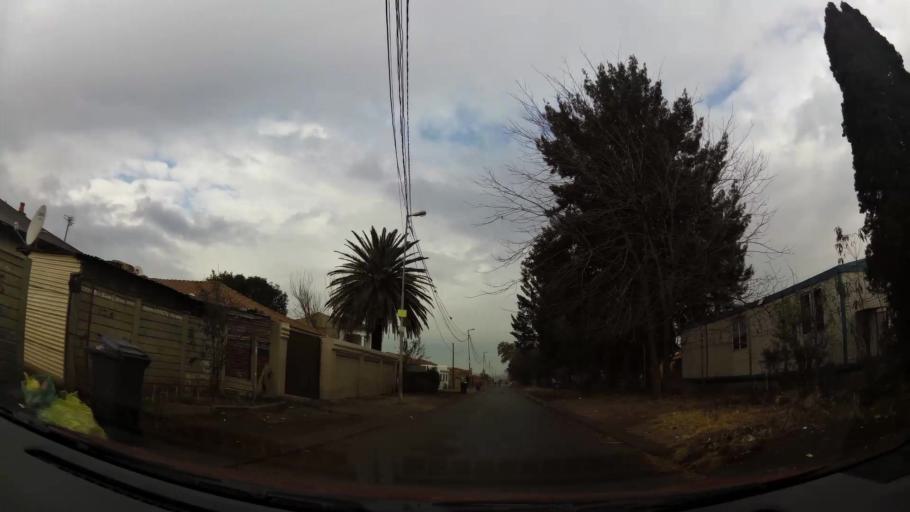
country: ZA
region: Gauteng
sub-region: City of Johannesburg Metropolitan Municipality
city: Soweto
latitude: -26.2810
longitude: 27.8406
